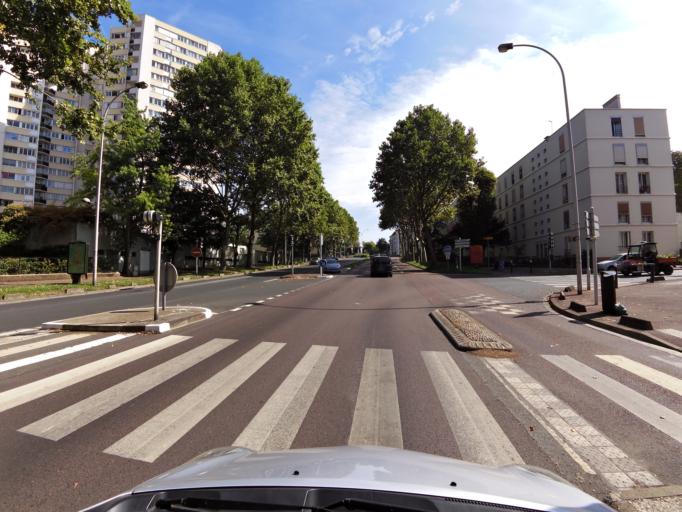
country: FR
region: Ile-de-France
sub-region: Departement du Val-de-Marne
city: Creteil
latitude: 48.7926
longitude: 2.4589
